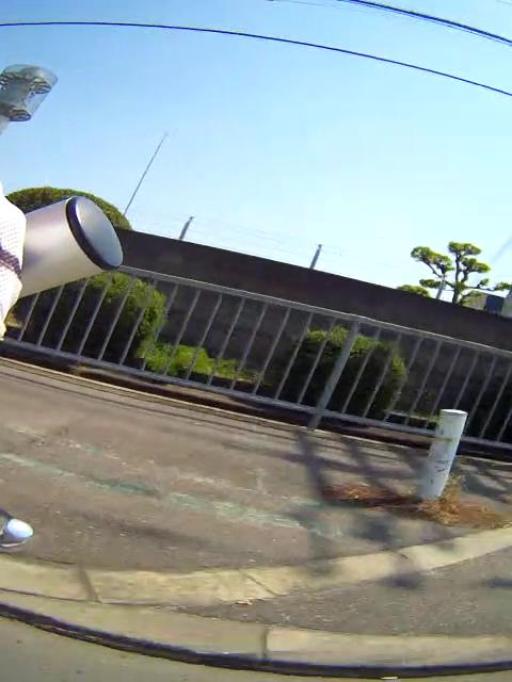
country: JP
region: Osaka
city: Matsubara
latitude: 34.5589
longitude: 135.5515
